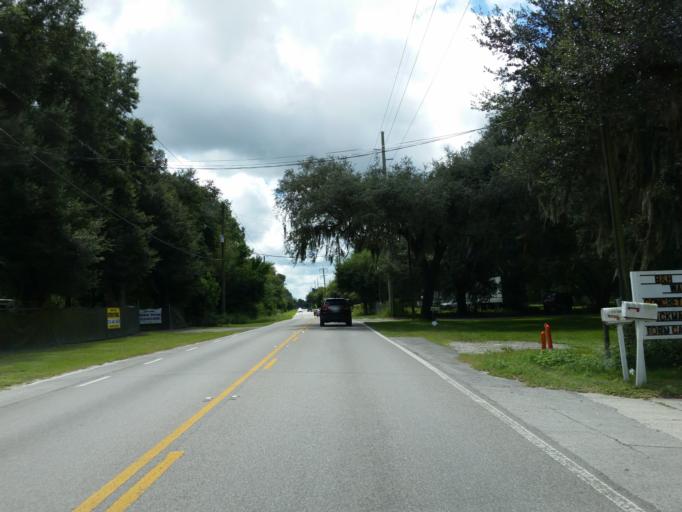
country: US
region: Florida
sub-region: Pasco County
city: Zephyrhills West
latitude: 28.2159
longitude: -82.2462
